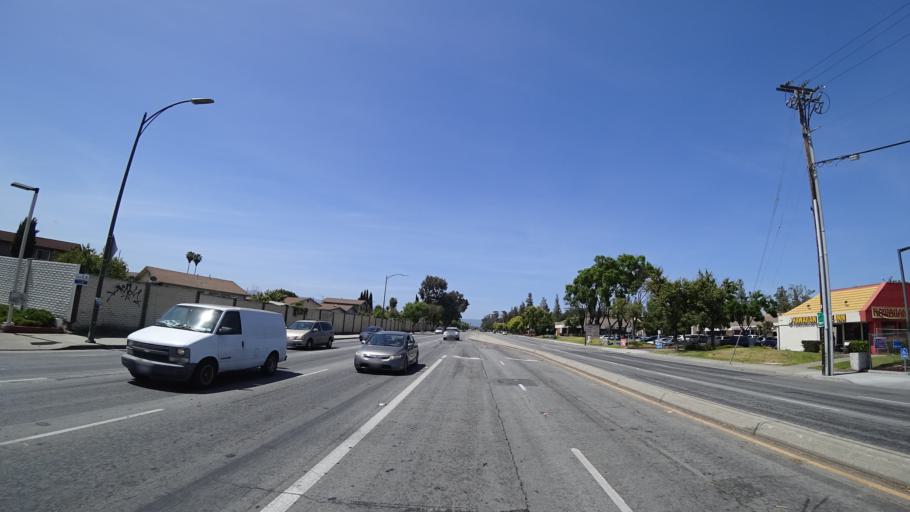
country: US
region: California
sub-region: Santa Clara County
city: Seven Trees
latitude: 37.3149
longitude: -121.8370
